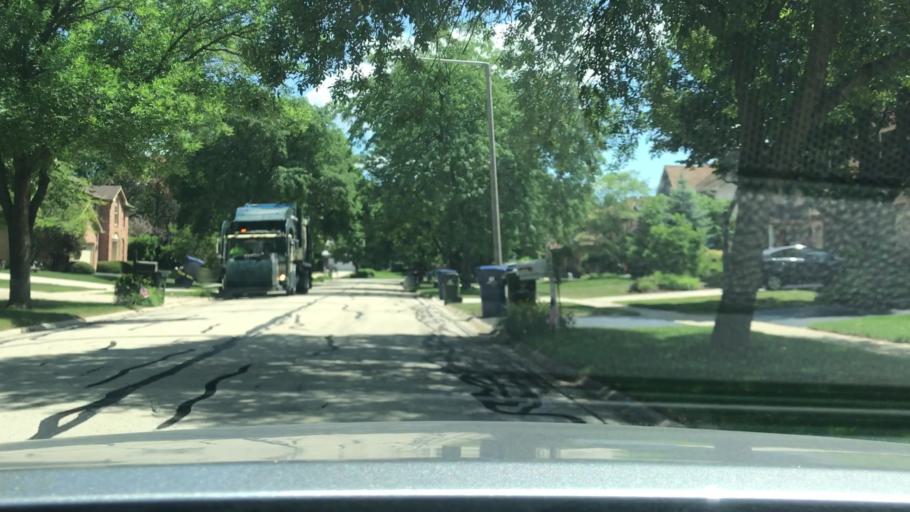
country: US
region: Illinois
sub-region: DuPage County
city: Naperville
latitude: 41.7572
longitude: -88.1062
